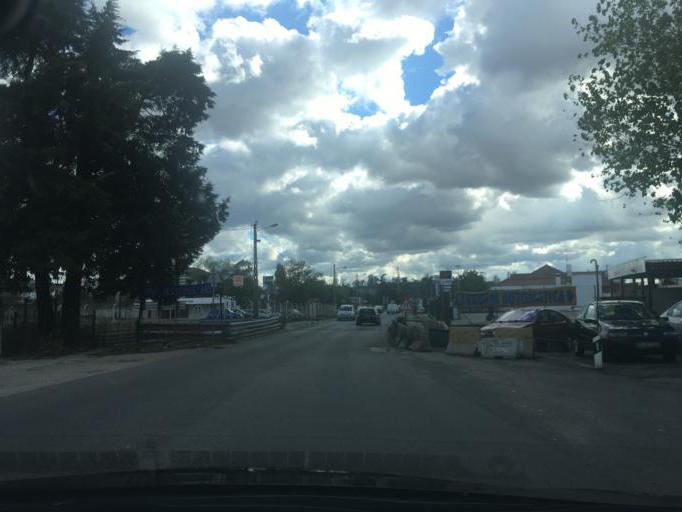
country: PT
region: Santarem
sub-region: Torres Novas
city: Riachos
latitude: 39.4651
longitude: -8.5234
